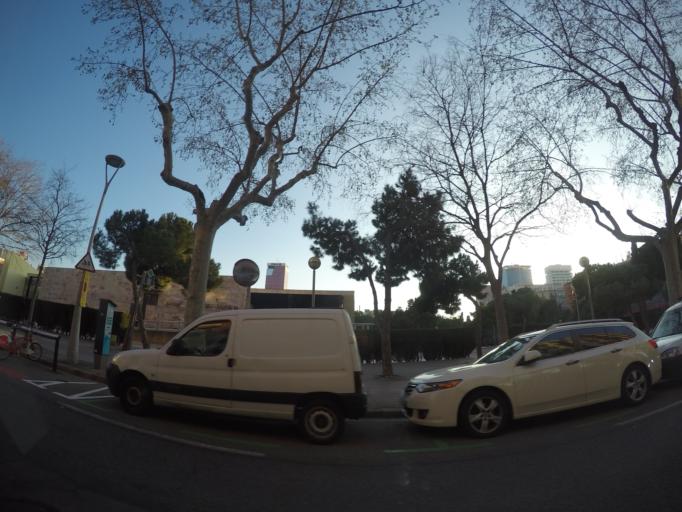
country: ES
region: Catalonia
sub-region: Provincia de Barcelona
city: Sants-Montjuic
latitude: 41.3793
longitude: 2.1488
